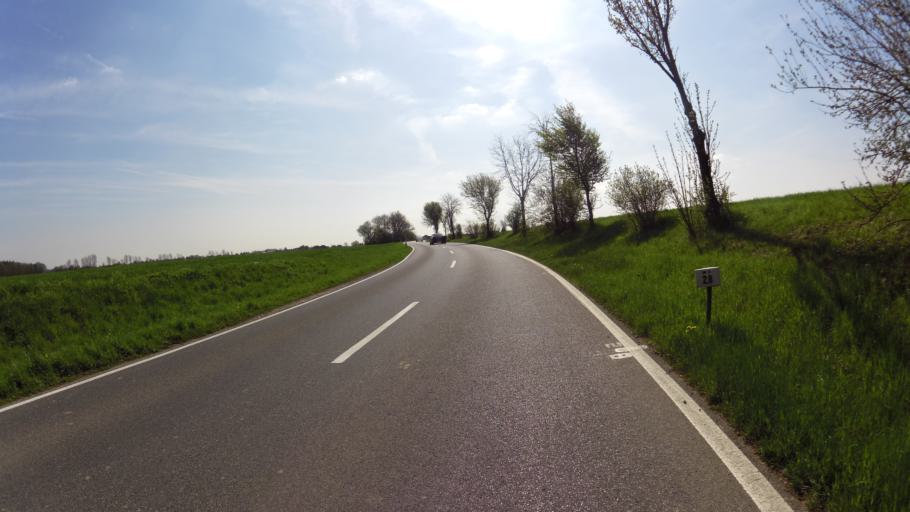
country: DE
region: North Rhine-Westphalia
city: Geilenkirchen
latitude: 50.9882
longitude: 6.0719
